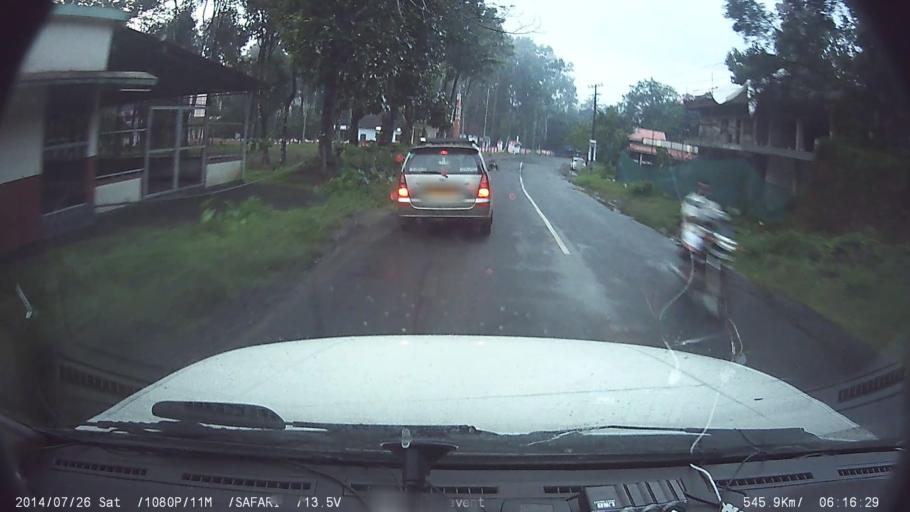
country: IN
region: Kerala
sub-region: Kottayam
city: Palackattumala
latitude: 9.8318
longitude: 76.5931
